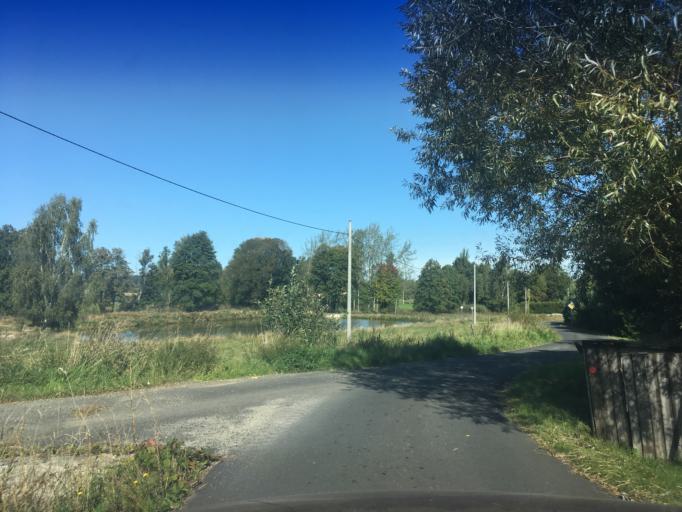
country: PL
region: Lower Silesian Voivodeship
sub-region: Powiat lubanski
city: Lesna
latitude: 51.0016
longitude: 15.1923
